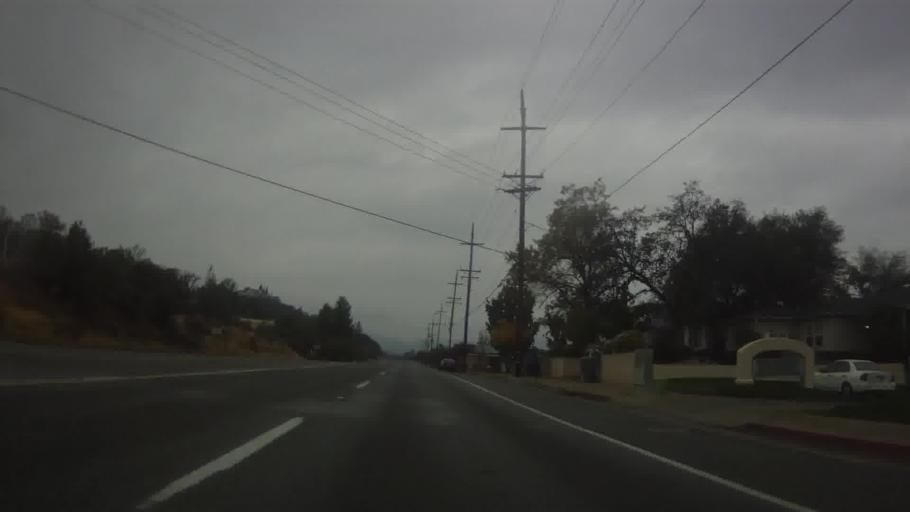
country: US
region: California
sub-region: Shasta County
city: Redding
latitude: 40.5861
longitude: -122.4108
